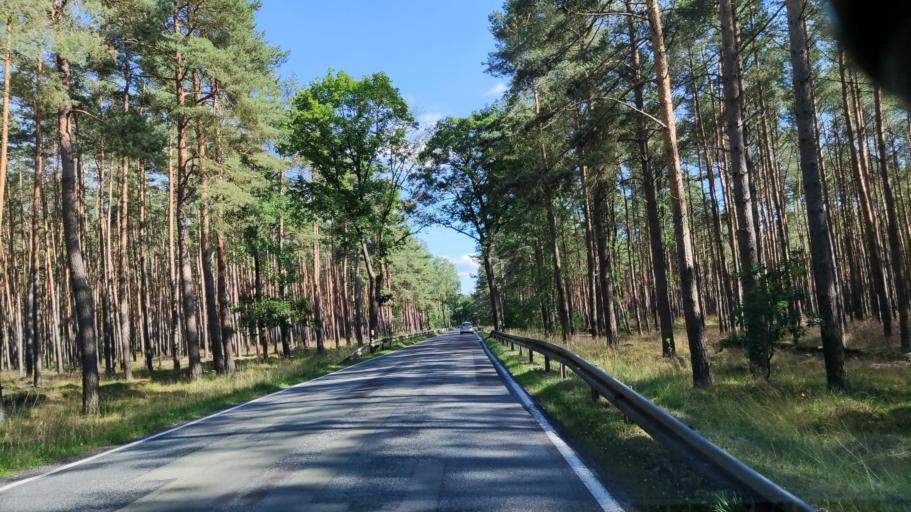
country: DE
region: Lower Saxony
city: Damnatz
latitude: 53.1926
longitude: 11.2080
